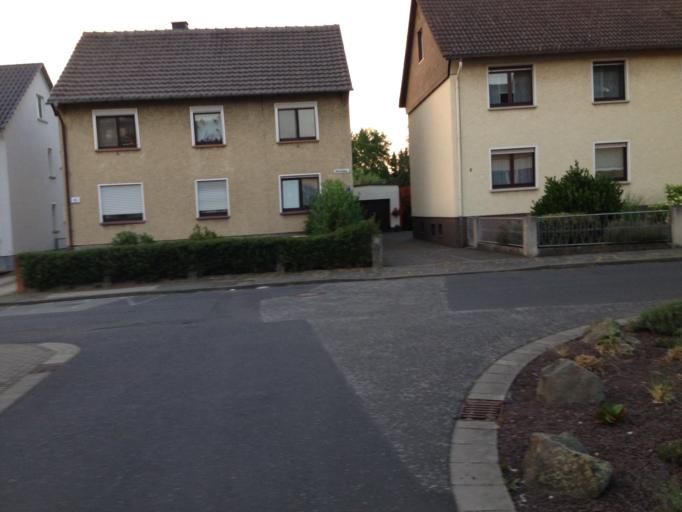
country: DE
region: Hesse
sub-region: Regierungsbezirk Giessen
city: Hoernsheim
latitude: 50.5332
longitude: 8.6516
